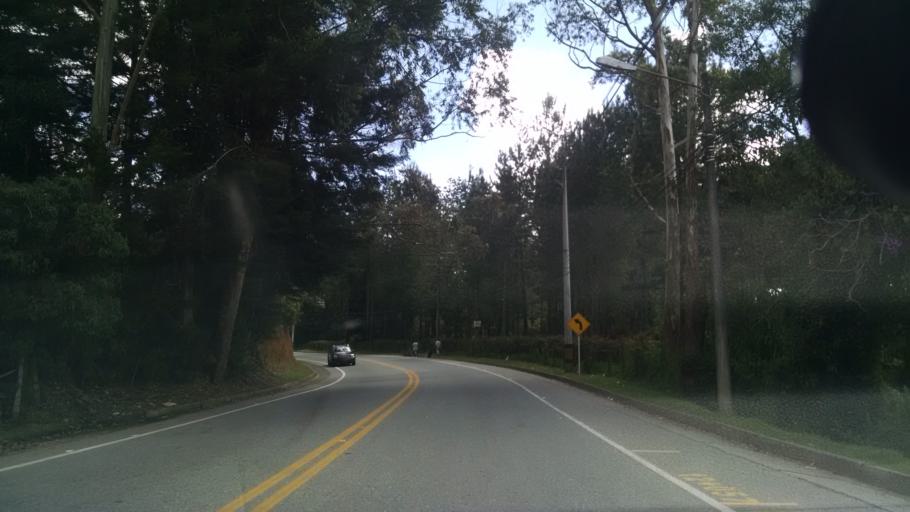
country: CO
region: Antioquia
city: Envigado
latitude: 6.1433
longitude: -75.5241
